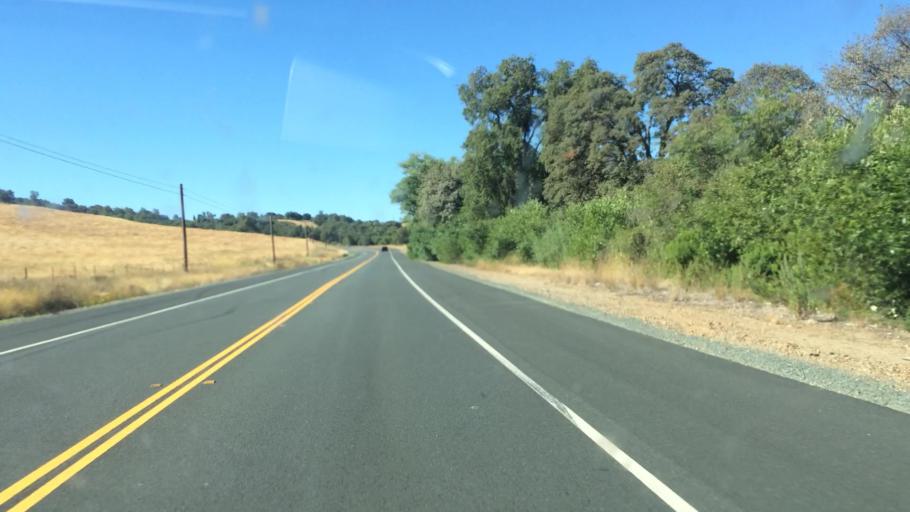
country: US
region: California
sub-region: El Dorado County
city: Deer Park
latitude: 38.6554
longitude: -120.8538
